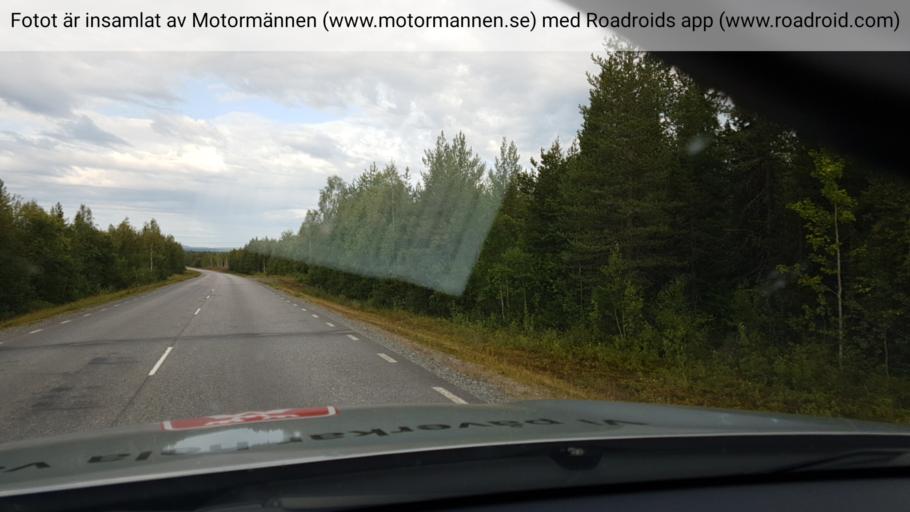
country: SE
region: Vaesterbotten
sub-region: Skelleftea Kommun
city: Storvik
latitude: 65.3704
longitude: 20.3953
